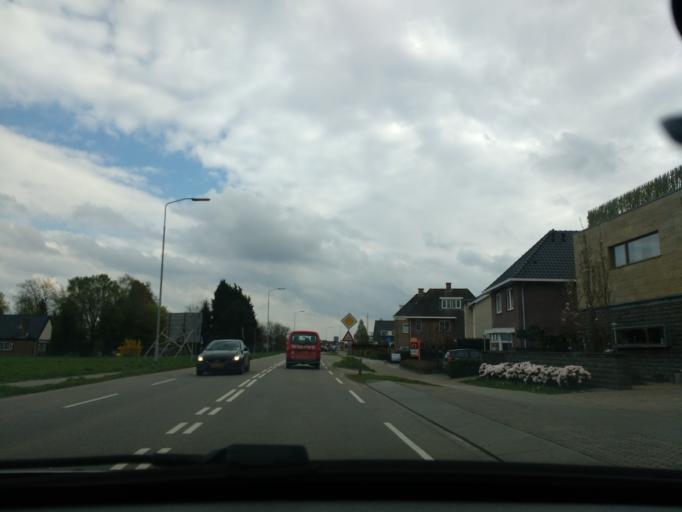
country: NL
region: Gelderland
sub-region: Gemeente Overbetuwe
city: Oosterhout
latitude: 51.8804
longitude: 5.8485
